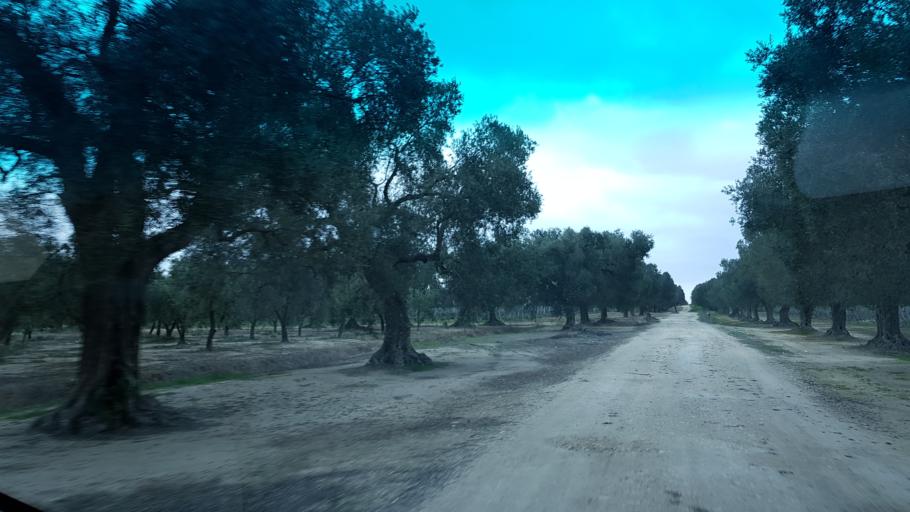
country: IT
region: Apulia
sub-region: Provincia di Brindisi
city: La Rosa
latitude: 40.5890
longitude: 17.9834
